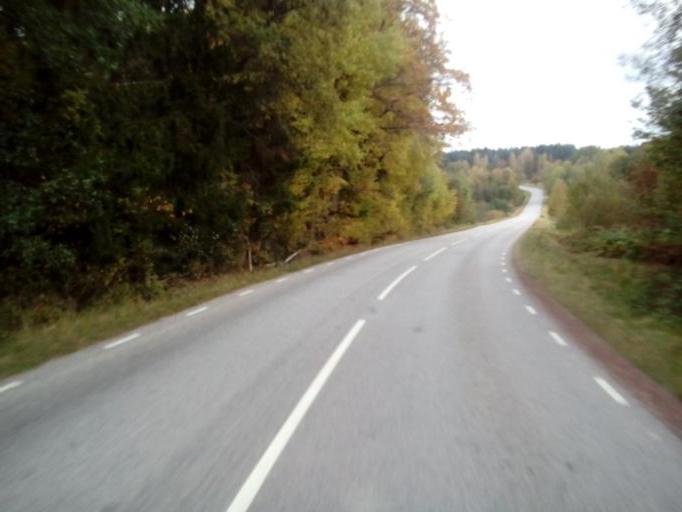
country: SE
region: Kalmar
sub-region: Vasterviks Kommun
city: Gamleby
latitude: 57.8779
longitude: 16.3152
